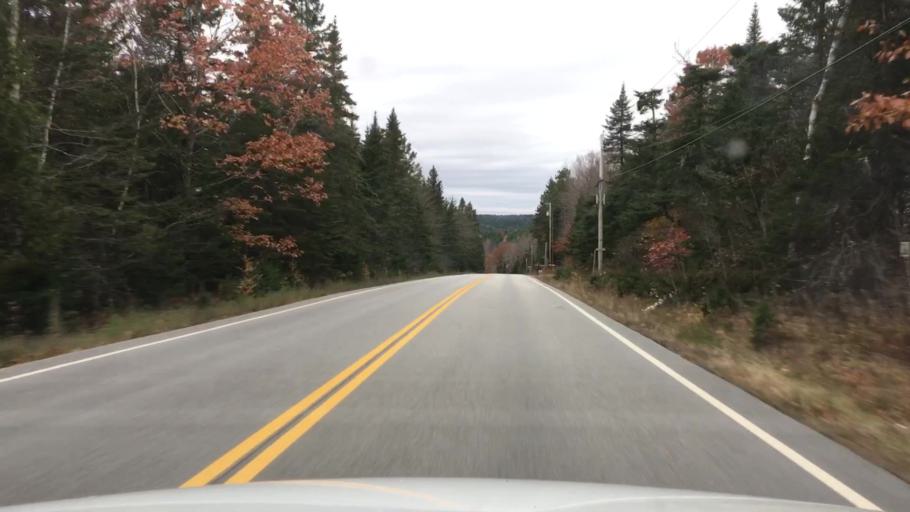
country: US
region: Maine
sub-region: Hancock County
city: Penobscot
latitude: 44.4969
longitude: -68.6469
